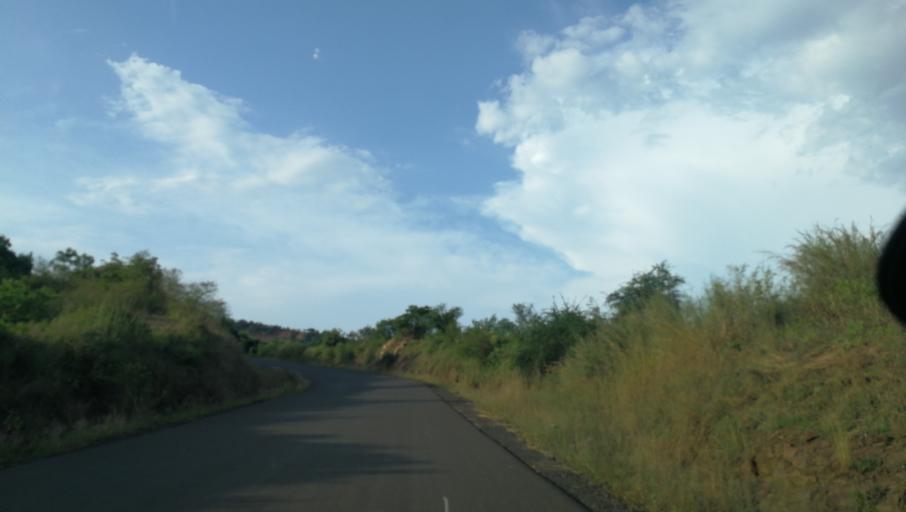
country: ET
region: Southern Nations, Nationalities, and People's Region
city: Areka
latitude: 6.8386
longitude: 37.2765
